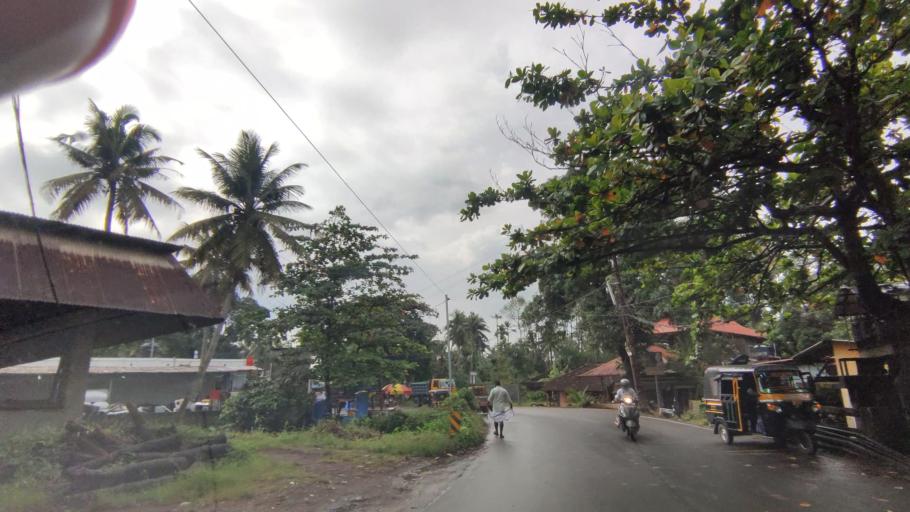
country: IN
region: Kerala
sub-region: Kottayam
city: Kottayam
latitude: 9.5886
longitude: 76.4915
